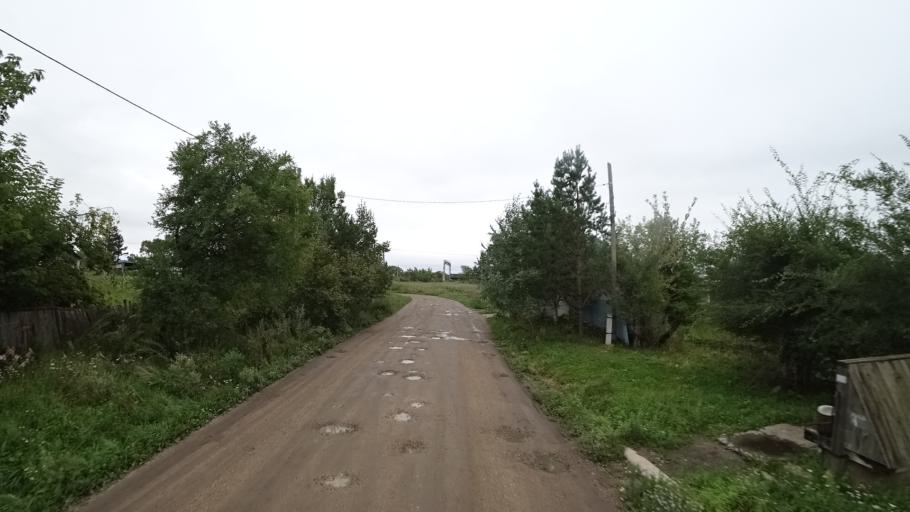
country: RU
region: Primorskiy
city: Chernigovka
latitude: 44.3434
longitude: 132.5345
